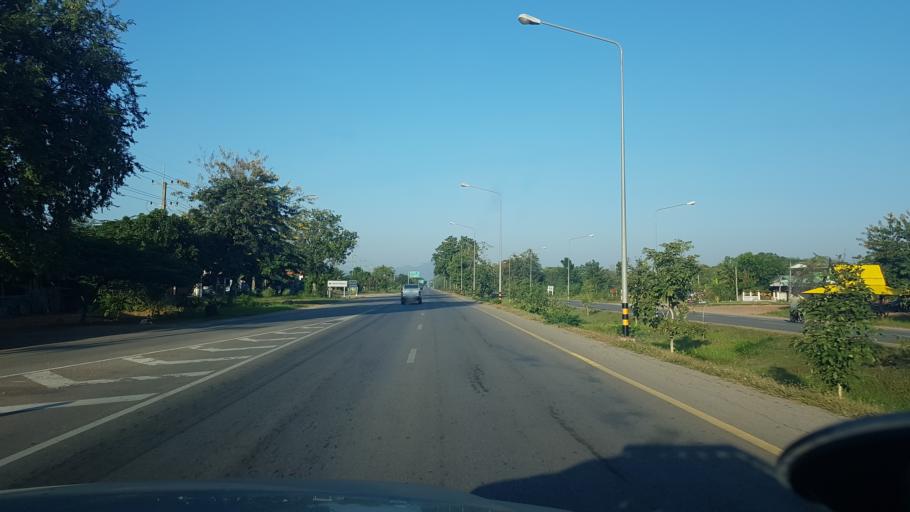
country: TH
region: Chaiyaphum
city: Khon San
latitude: 16.5895
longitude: 101.9956
